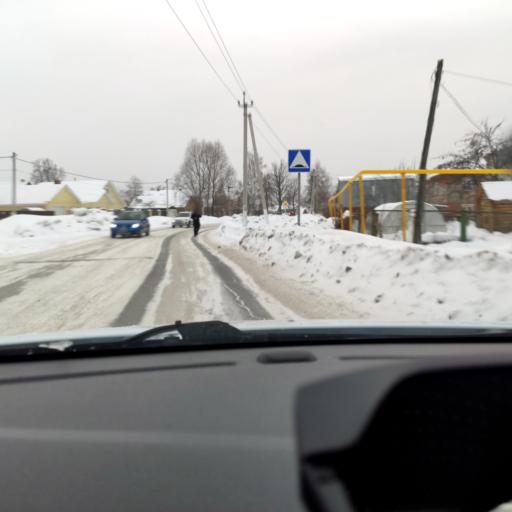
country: RU
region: Tatarstan
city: Vysokaya Gora
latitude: 55.9351
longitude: 49.3136
